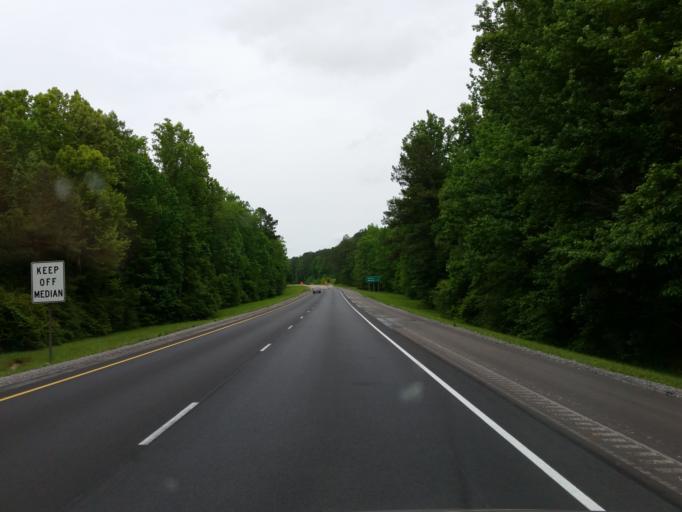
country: US
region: Mississippi
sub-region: Clarke County
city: Stonewall
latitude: 31.9722
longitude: -88.9587
